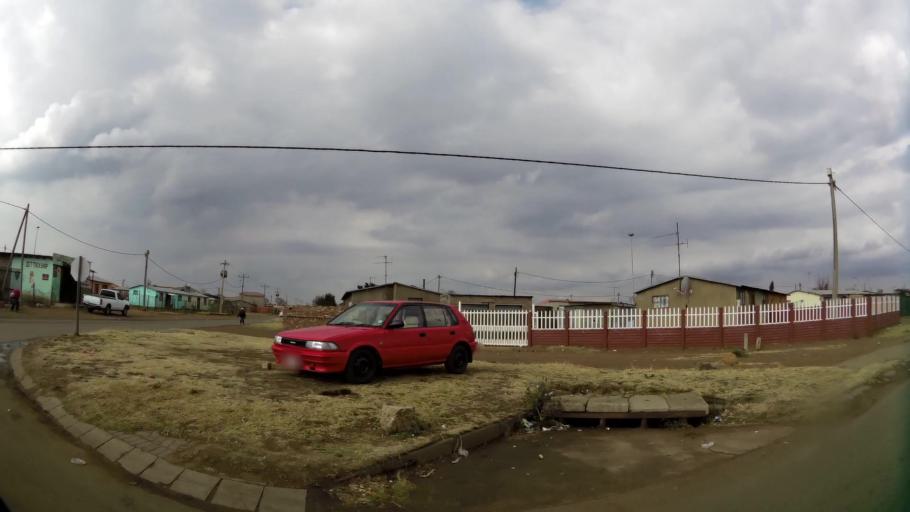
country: ZA
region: Gauteng
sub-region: Sedibeng District Municipality
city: Vanderbijlpark
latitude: -26.6964
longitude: 27.7907
